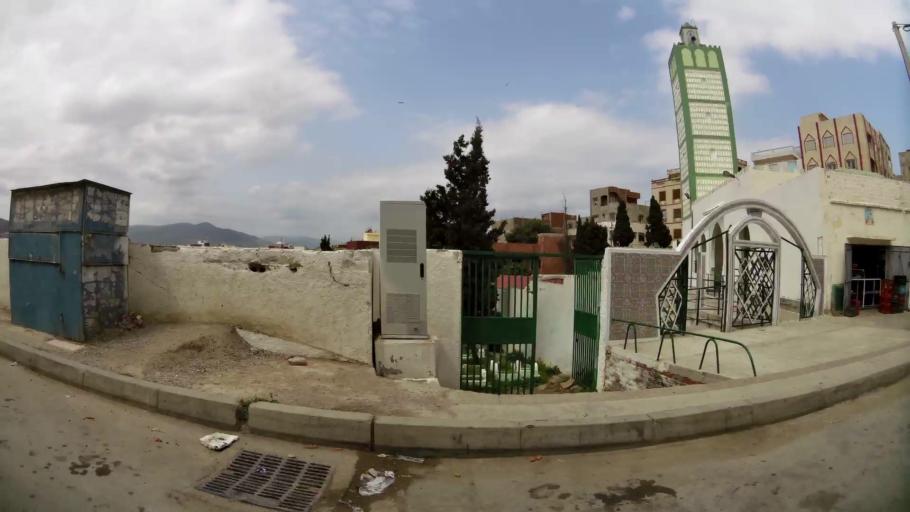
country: MA
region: Tanger-Tetouan
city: Tetouan
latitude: 35.5705
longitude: -5.3959
